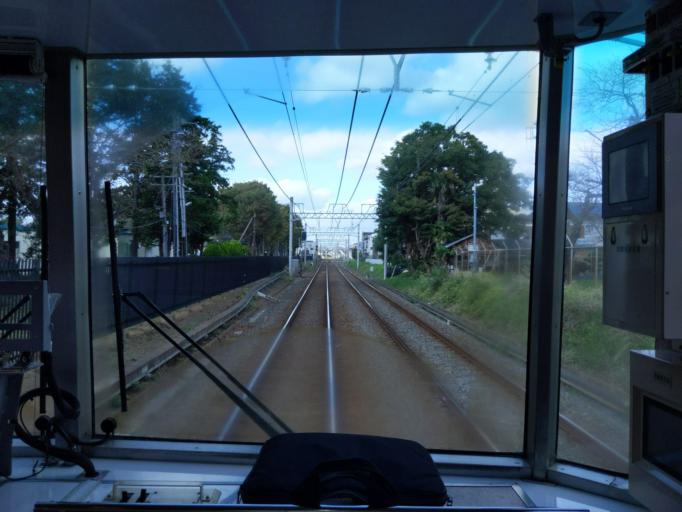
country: JP
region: Chiba
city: Kashiwa
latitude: 35.7854
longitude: 139.9765
